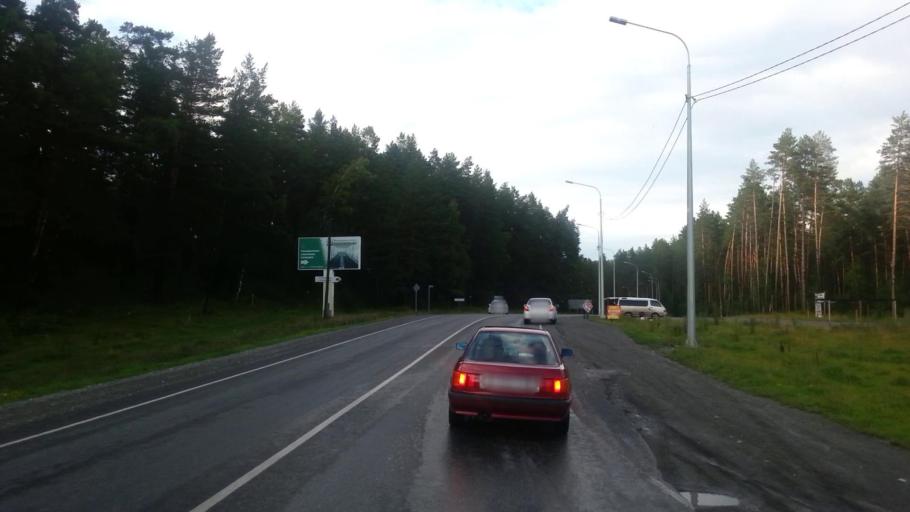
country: RU
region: Altay
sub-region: Mayminskiy Rayon
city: Manzherok
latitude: 51.8214
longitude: 85.7860
